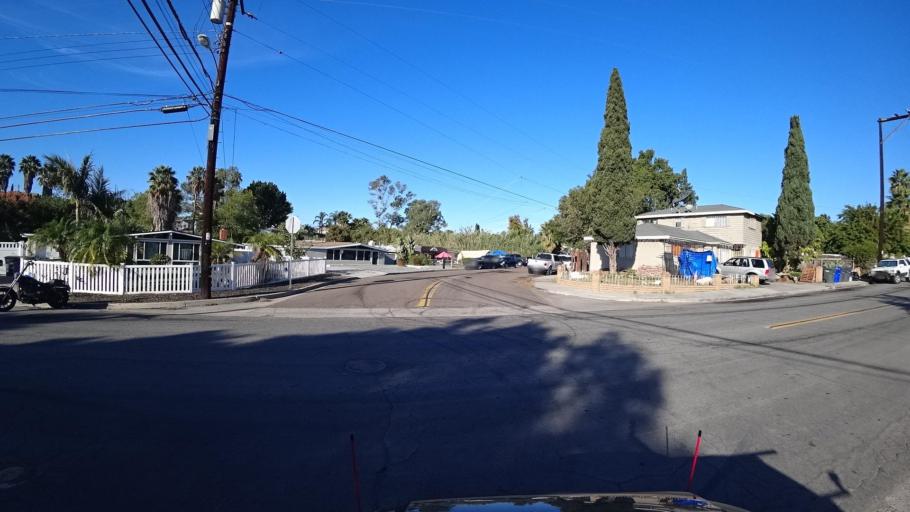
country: US
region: California
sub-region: San Diego County
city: La Presa
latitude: 32.7101
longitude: -116.9885
